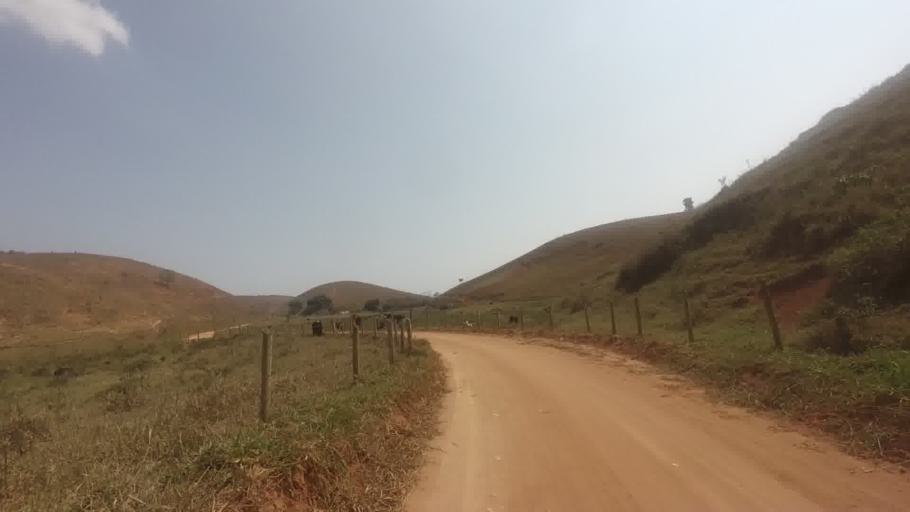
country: BR
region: Espirito Santo
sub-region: Sao Jose Do Calcado
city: Sao Jose do Calcado
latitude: -21.0587
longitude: -41.5367
